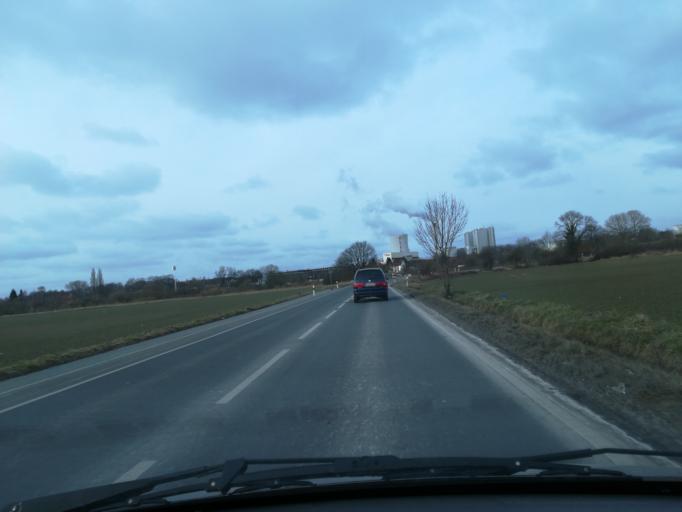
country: DE
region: Lower Saxony
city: Auf der Horst
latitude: 52.4103
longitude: 9.6464
